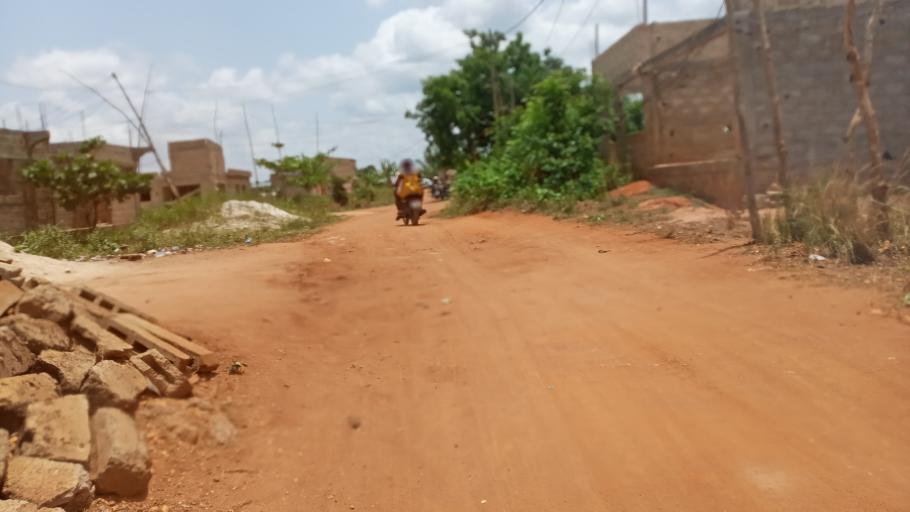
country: TG
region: Maritime
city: Tsevie
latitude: 6.2930
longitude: 1.1344
